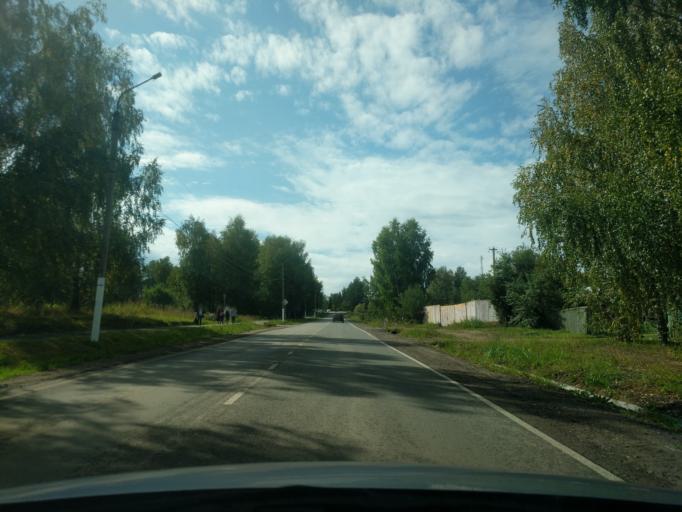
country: RU
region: Kostroma
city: Sudislavl'
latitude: 57.8803
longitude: 41.6940
